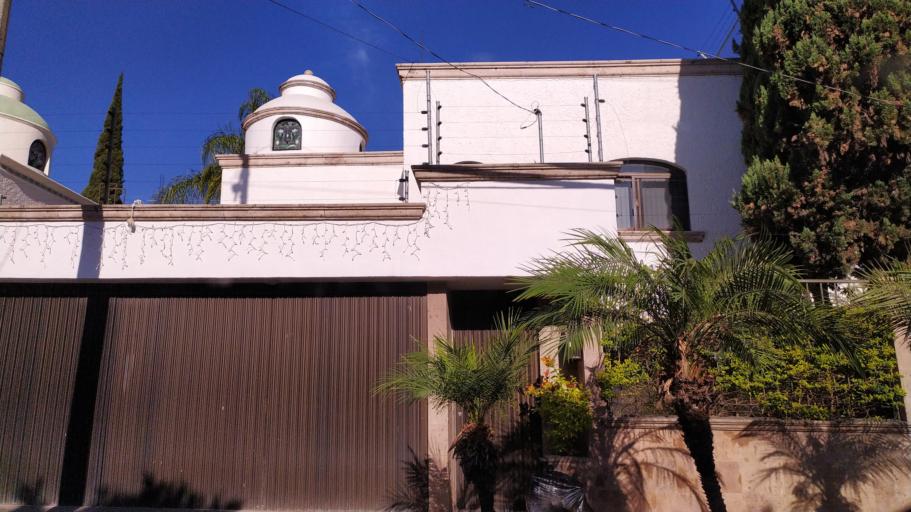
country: MX
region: Jalisco
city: Guadalajara
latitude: 20.6625
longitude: -103.4266
